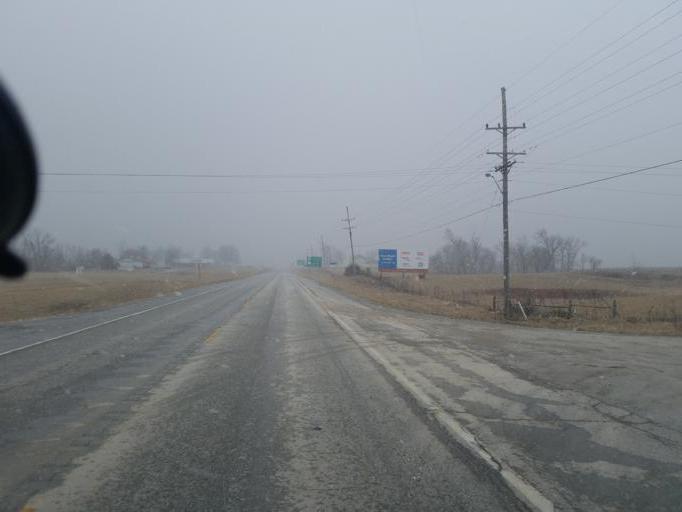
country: US
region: Missouri
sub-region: Adair County
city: Kirksville
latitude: 40.2500
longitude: -92.5826
